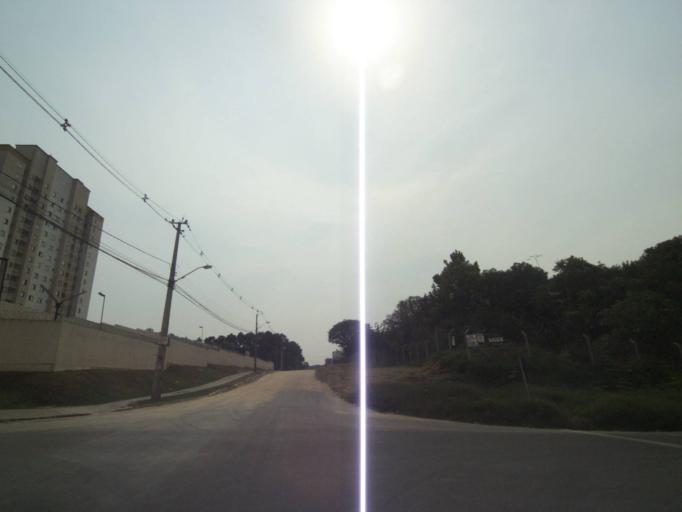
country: BR
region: Parana
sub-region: Sao Jose Dos Pinhais
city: Sao Jose dos Pinhais
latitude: -25.5165
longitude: -49.2873
